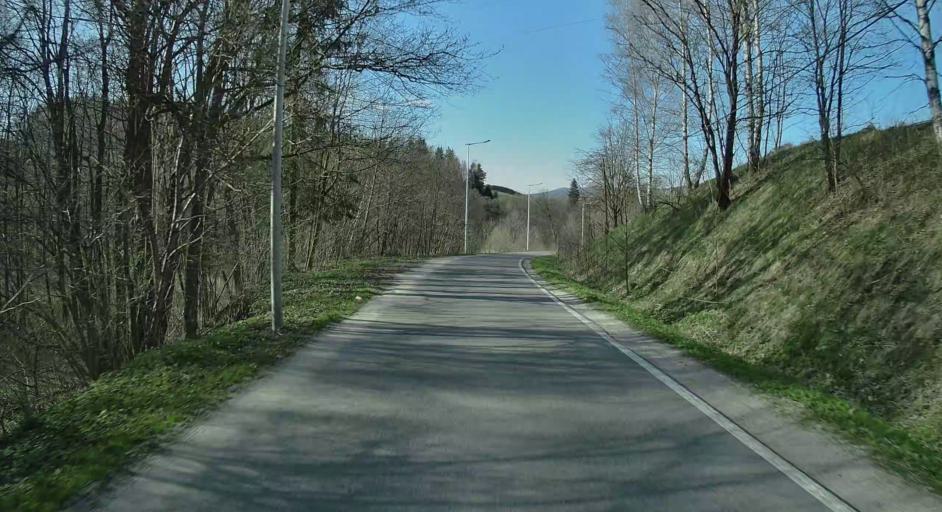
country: PL
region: Lower Silesian Voivodeship
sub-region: Powiat klodzki
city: Lewin Klodzki
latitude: 50.3891
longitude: 16.3003
